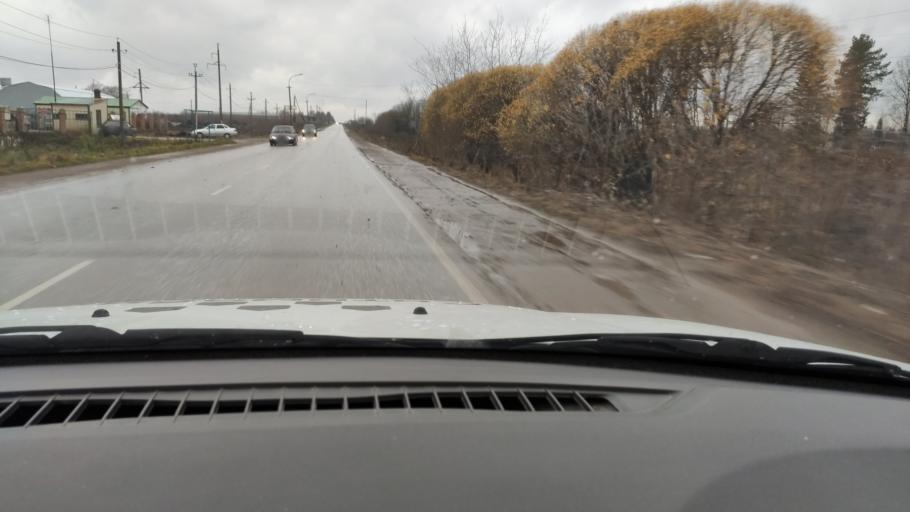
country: RU
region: Perm
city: Sylva
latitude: 58.0266
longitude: 56.7309
